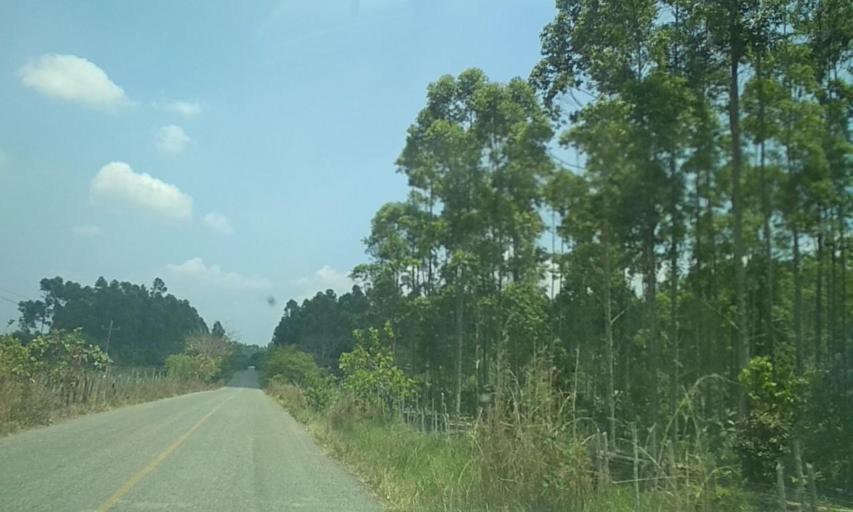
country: MX
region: Tabasco
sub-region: Huimanguillo
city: Francisco Rueda
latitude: 17.8422
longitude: -93.8956
